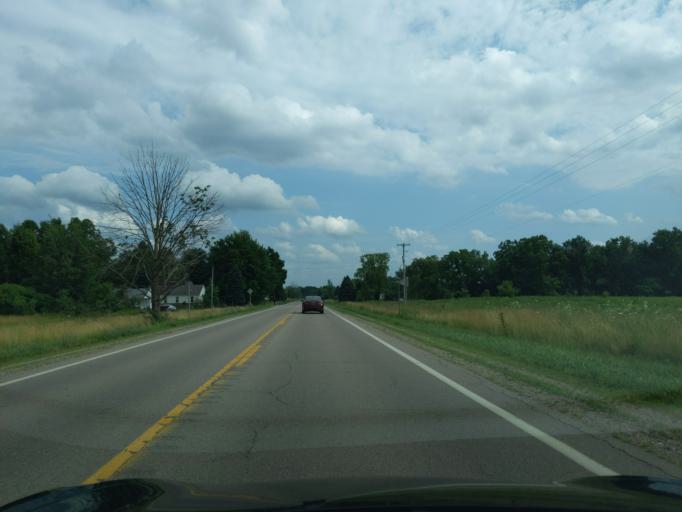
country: US
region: Michigan
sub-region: Eaton County
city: Eaton Rapids
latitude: 42.4560
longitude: -84.6538
